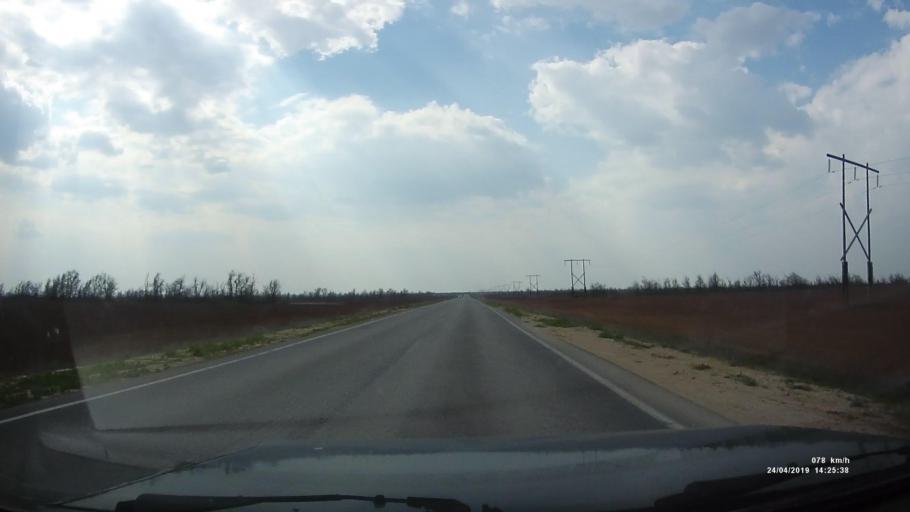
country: RU
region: Kalmykiya
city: Arshan'
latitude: 46.3315
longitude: 44.0786
